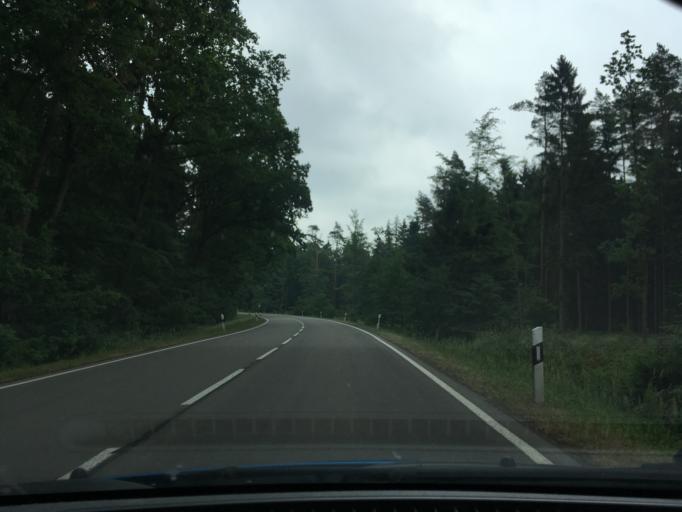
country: DE
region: Lower Saxony
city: Zernien
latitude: 53.0690
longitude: 10.9199
